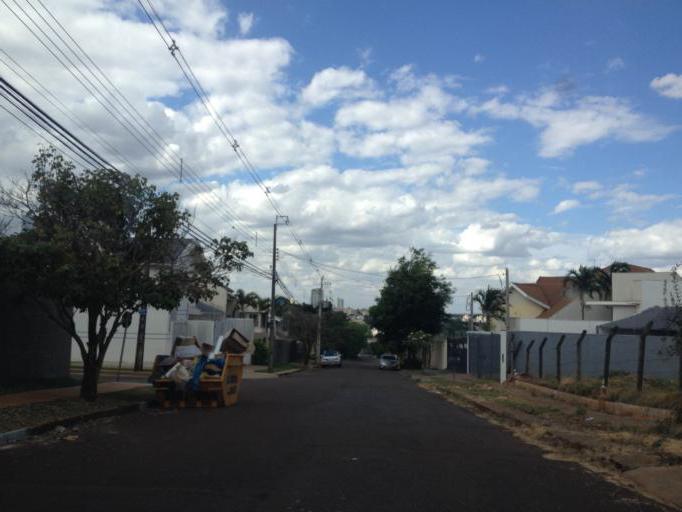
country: BR
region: Parana
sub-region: Maringa
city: Maringa
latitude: -23.4466
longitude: -51.9487
